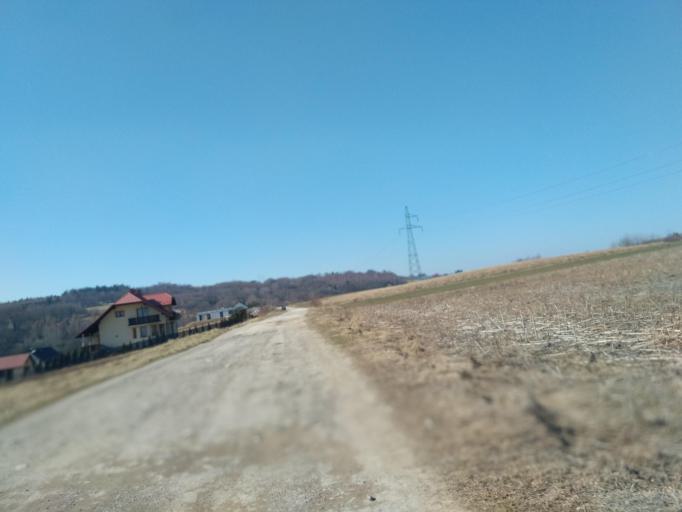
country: PL
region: Subcarpathian Voivodeship
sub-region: Powiat rzeszowski
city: Niechobrz
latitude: 49.9759
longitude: 21.8611
